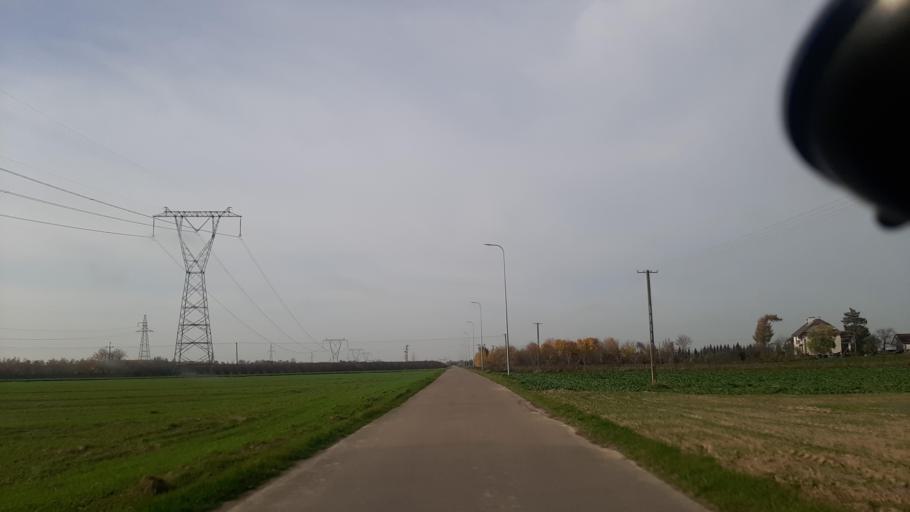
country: PL
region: Lublin Voivodeship
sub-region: Powiat lubelski
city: Lublin
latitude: 51.3335
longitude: 22.5334
